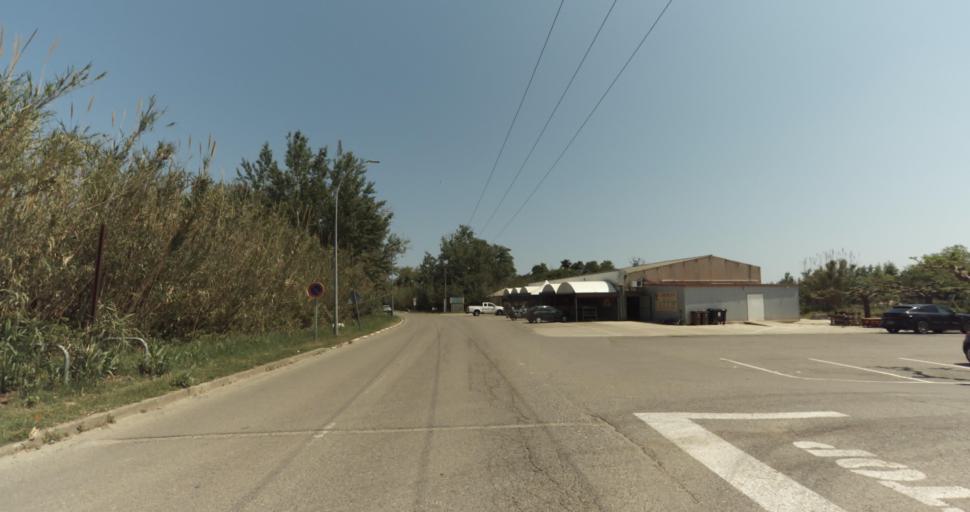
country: FR
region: Corsica
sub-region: Departement de la Haute-Corse
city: Biguglia
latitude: 42.6545
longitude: 9.4459
